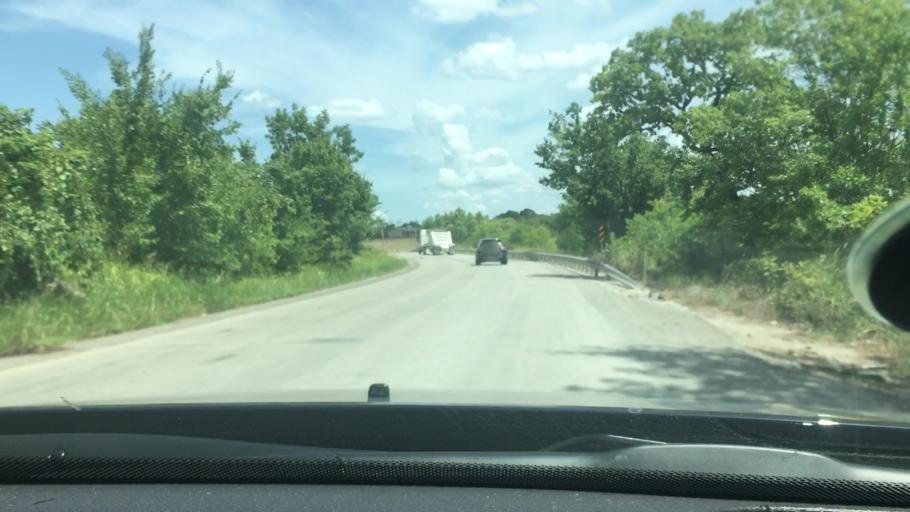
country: US
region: Oklahoma
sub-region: Carter County
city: Ardmore
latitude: 34.0755
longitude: -97.1699
